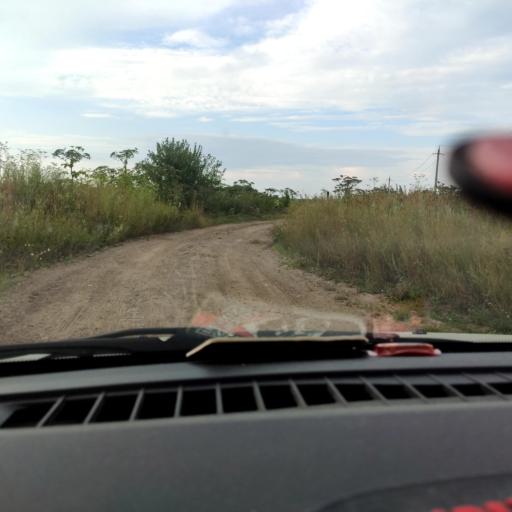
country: RU
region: Perm
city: Kultayevo
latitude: 57.8546
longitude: 55.9680
